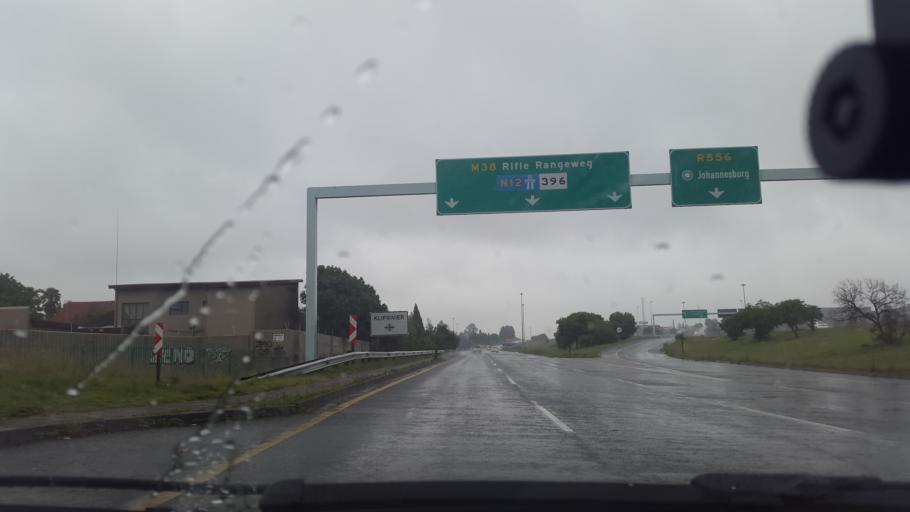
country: ZA
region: Gauteng
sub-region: City of Johannesburg Metropolitan Municipality
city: Johannesburg
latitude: -26.2703
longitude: 28.0314
